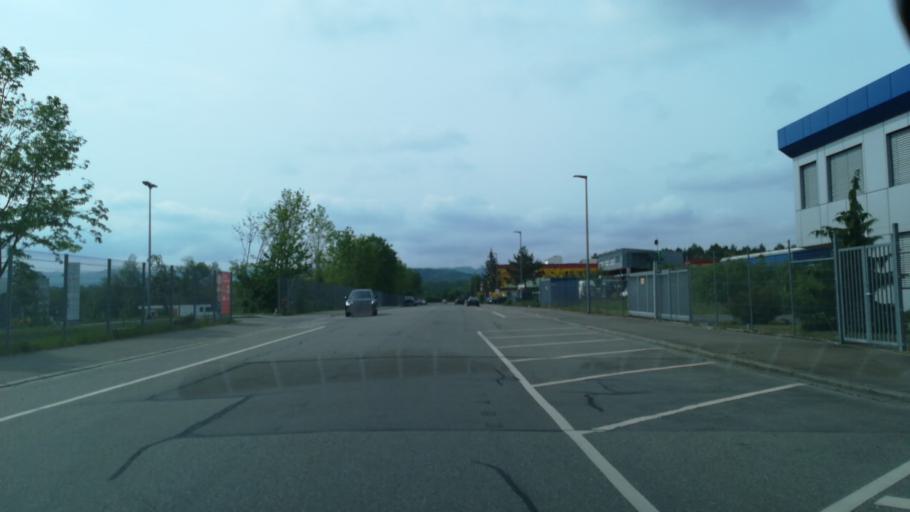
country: DE
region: Baden-Wuerttemberg
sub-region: Freiburg Region
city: Singen
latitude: 47.7557
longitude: 8.8728
